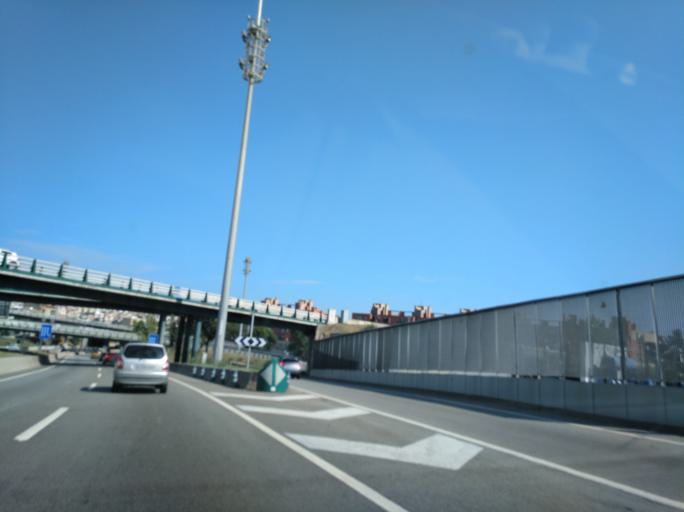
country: ES
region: Catalonia
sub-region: Provincia de Barcelona
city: Santa Coloma de Gramenet
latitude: 41.4495
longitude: 2.1972
